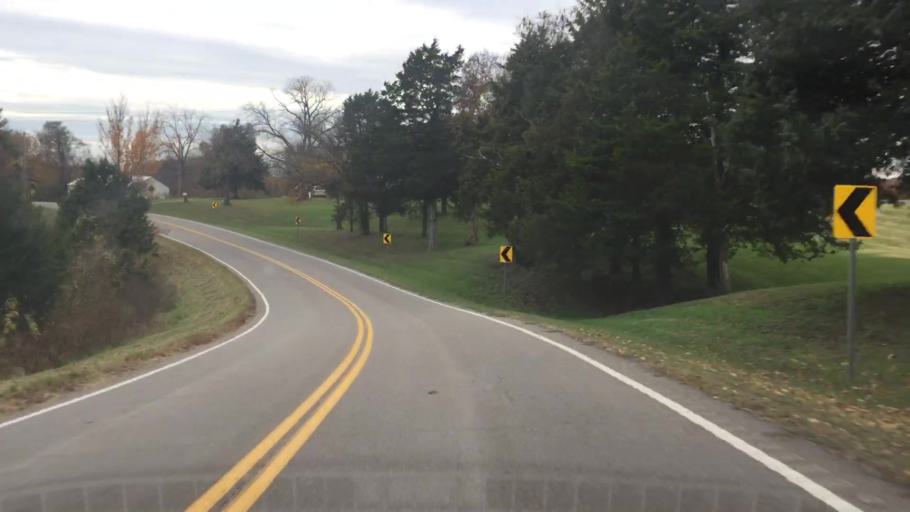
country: US
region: Missouri
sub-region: Osage County
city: Linn
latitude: 38.7148
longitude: -91.7123
